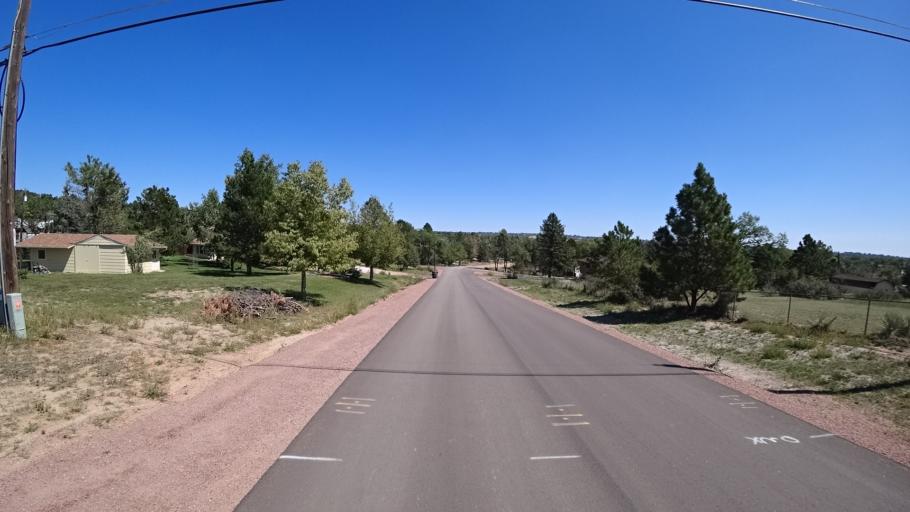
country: US
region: Colorado
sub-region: El Paso County
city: Cimarron Hills
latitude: 38.8625
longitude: -104.7373
